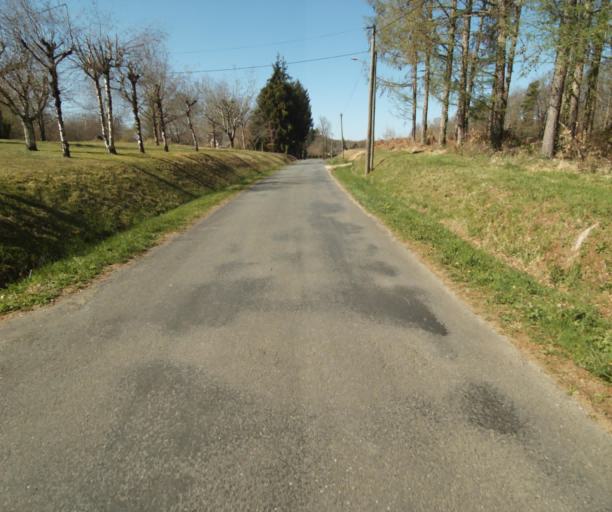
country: FR
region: Limousin
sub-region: Departement de la Correze
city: Chameyrat
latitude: 45.2834
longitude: 1.7134
